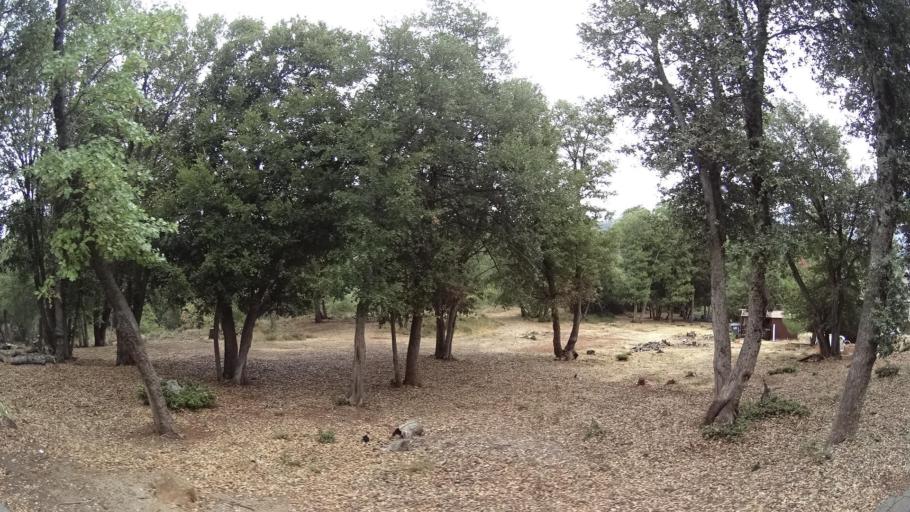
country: US
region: California
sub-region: San Diego County
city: Julian
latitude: 33.0427
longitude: -116.6248
